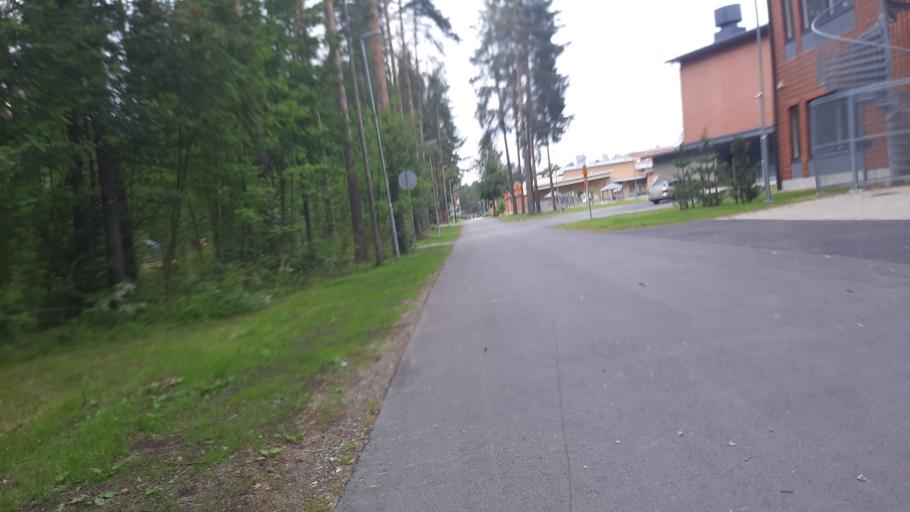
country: FI
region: North Karelia
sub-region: Joensuu
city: Joensuu
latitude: 62.6124
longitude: 29.8196
